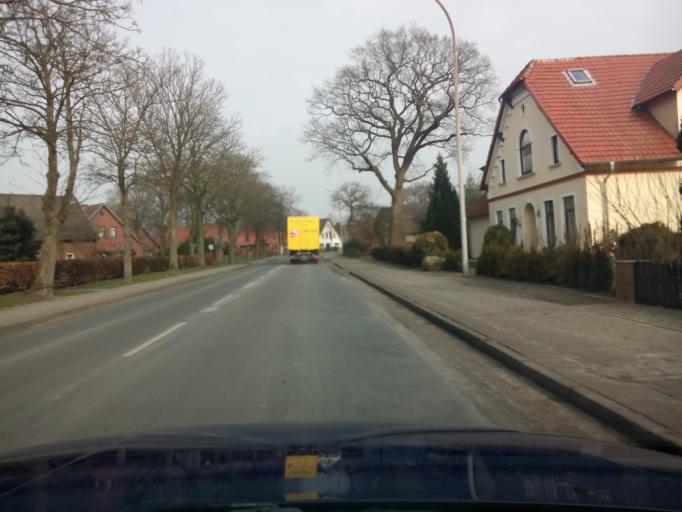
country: DE
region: Lower Saxony
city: Langen
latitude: 53.6201
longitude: 8.6344
